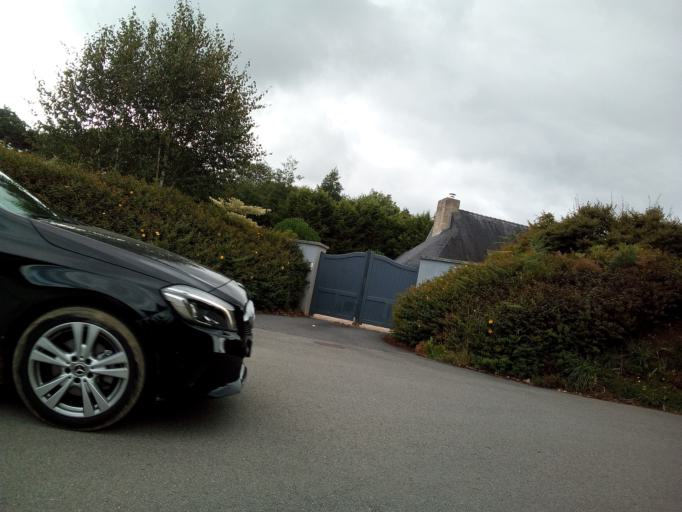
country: FR
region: Brittany
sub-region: Departement du Finistere
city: Landivisiau
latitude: 48.5116
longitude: -4.0571
